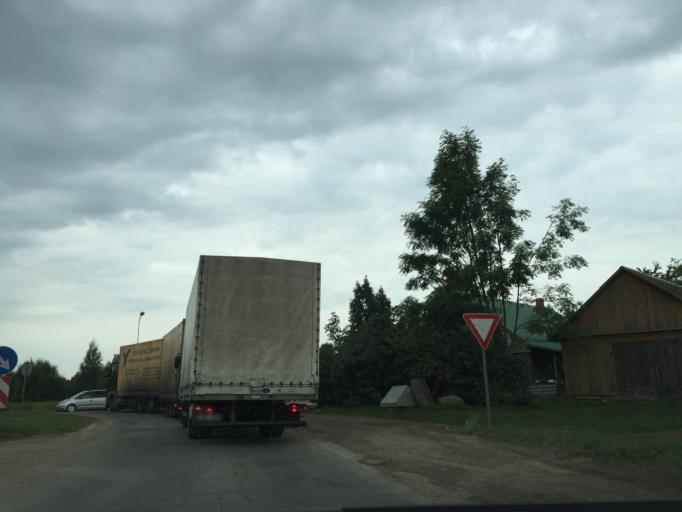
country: LV
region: Ludzas Rajons
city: Ludza
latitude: 56.5374
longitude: 27.6983
